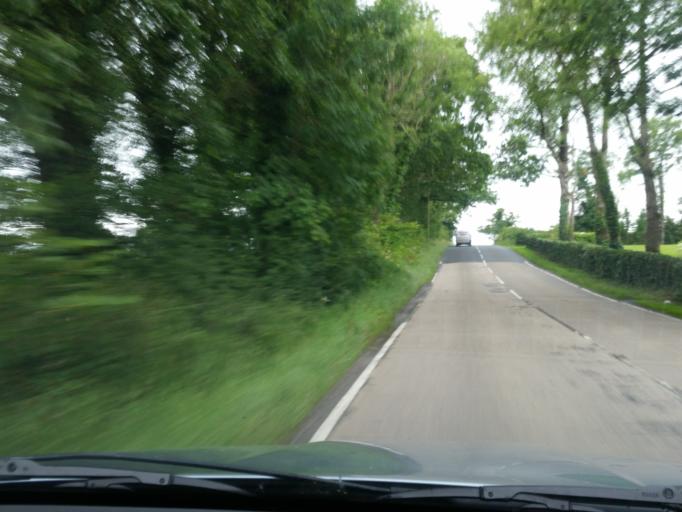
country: IE
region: Ulster
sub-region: An Cabhan
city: Ballyconnell
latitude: 54.1892
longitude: -7.5372
